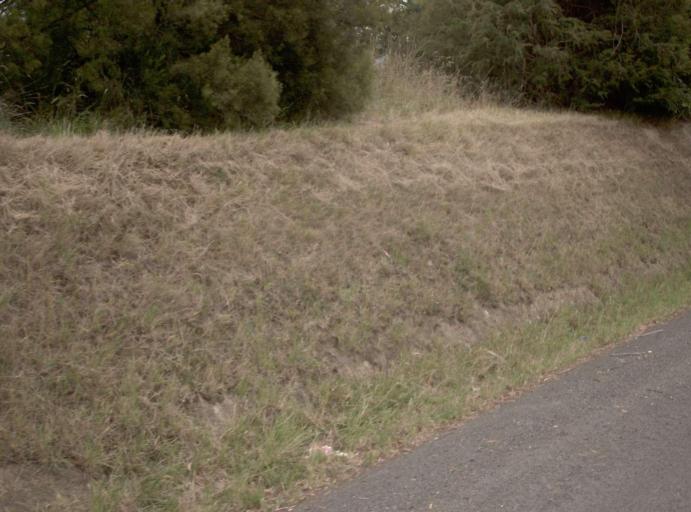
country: AU
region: Victoria
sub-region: Yarra Ranges
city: Launching Place
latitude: -37.7766
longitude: 145.5737
